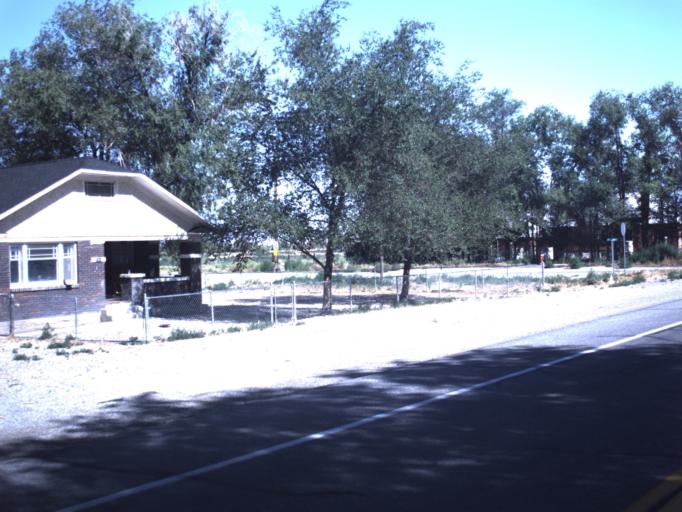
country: US
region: Utah
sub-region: Millard County
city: Delta
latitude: 39.2863
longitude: -112.6527
